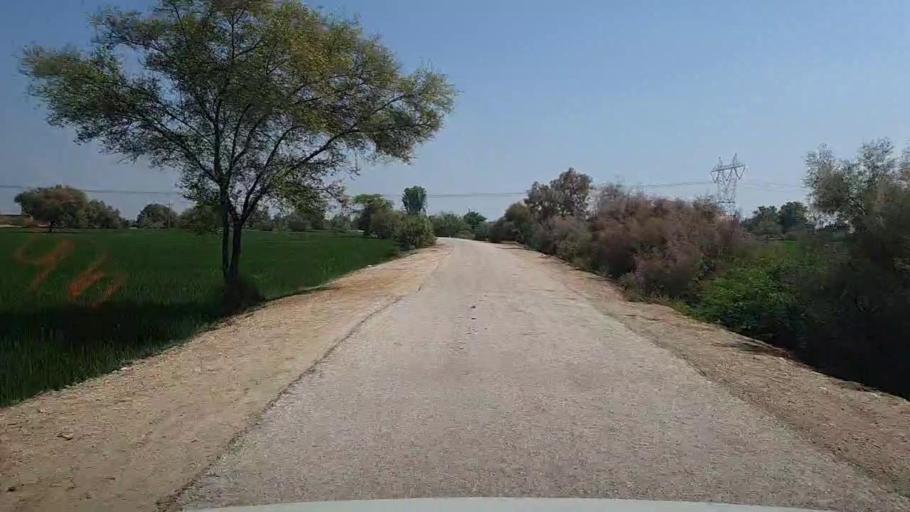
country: PK
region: Sindh
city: Kandhkot
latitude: 28.3067
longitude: 69.3428
